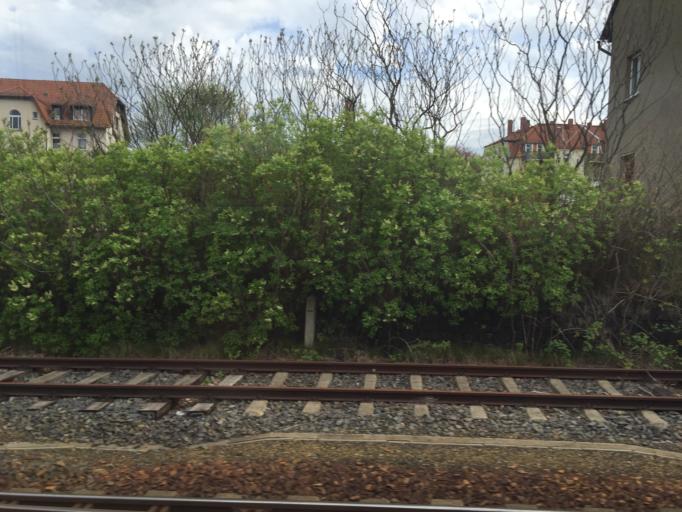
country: DE
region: Saxony
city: Bautzen
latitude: 51.1715
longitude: 14.4319
